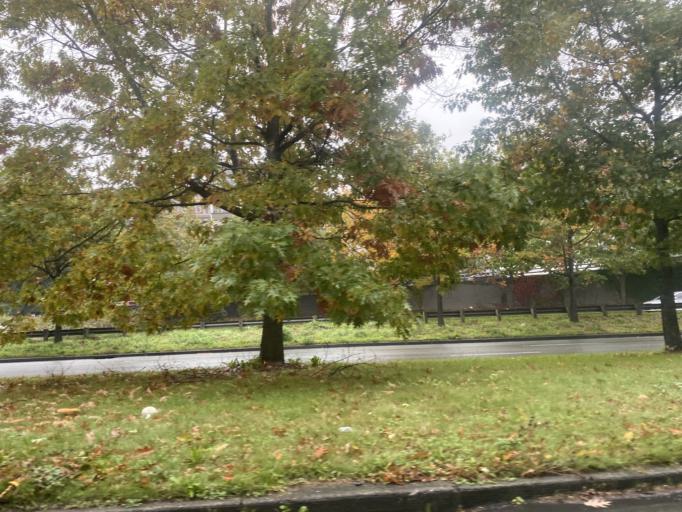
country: US
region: Washington
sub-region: King County
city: Seattle
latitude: 47.6496
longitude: -122.3767
